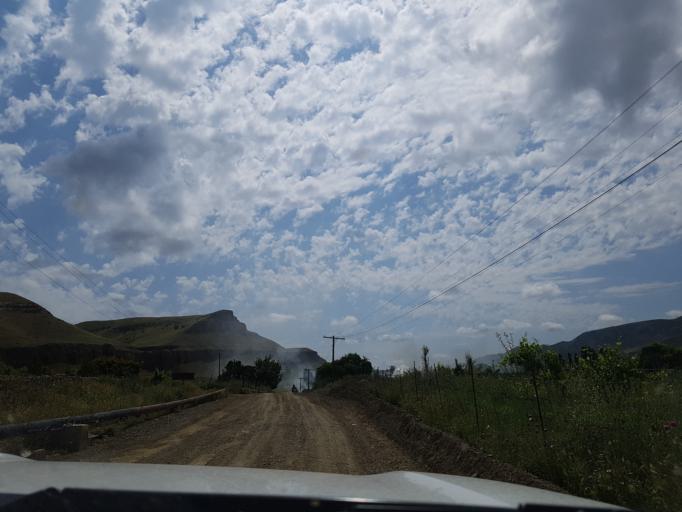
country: TM
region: Ahal
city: Baharly
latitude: 38.2265
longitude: 56.8760
